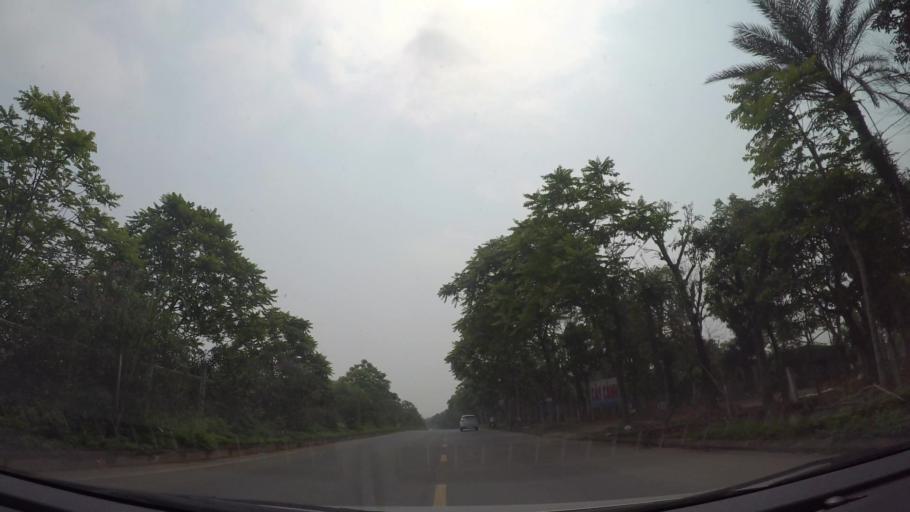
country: VN
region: Ha Noi
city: Lien Quan
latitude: 20.9886
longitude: 105.5701
